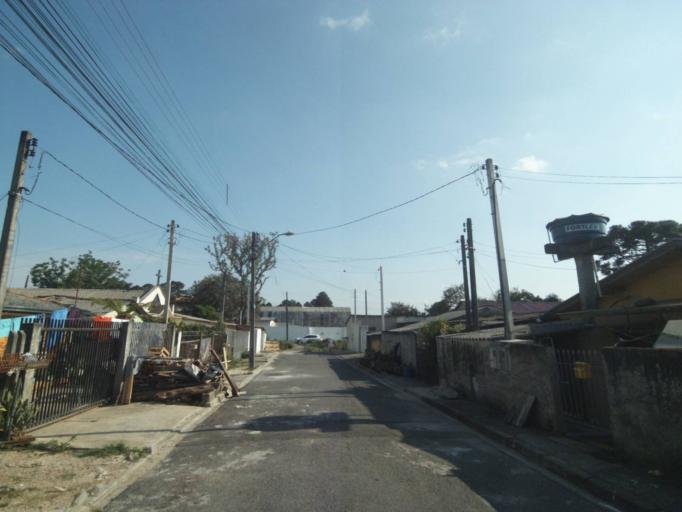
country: BR
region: Parana
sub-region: Curitiba
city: Curitiba
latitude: -25.4907
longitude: -49.3325
